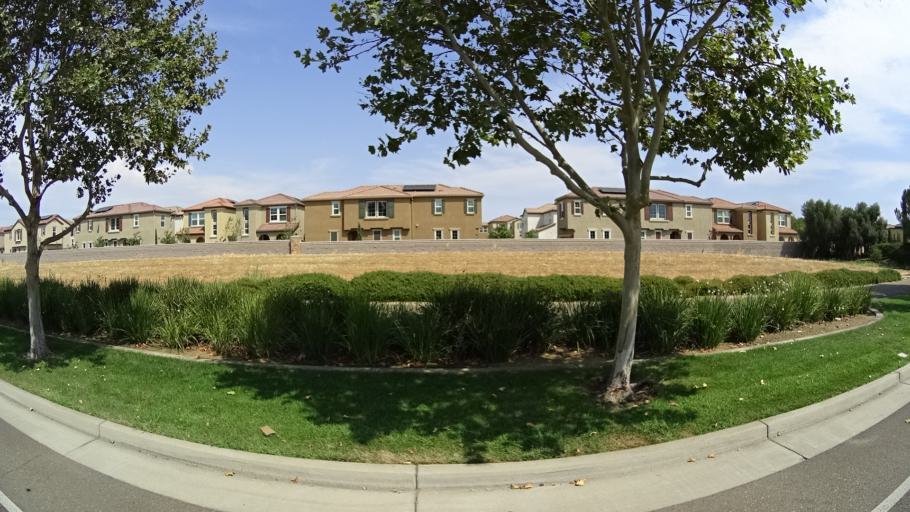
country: US
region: California
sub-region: Sacramento County
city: Laguna
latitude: 38.3937
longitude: -121.4498
